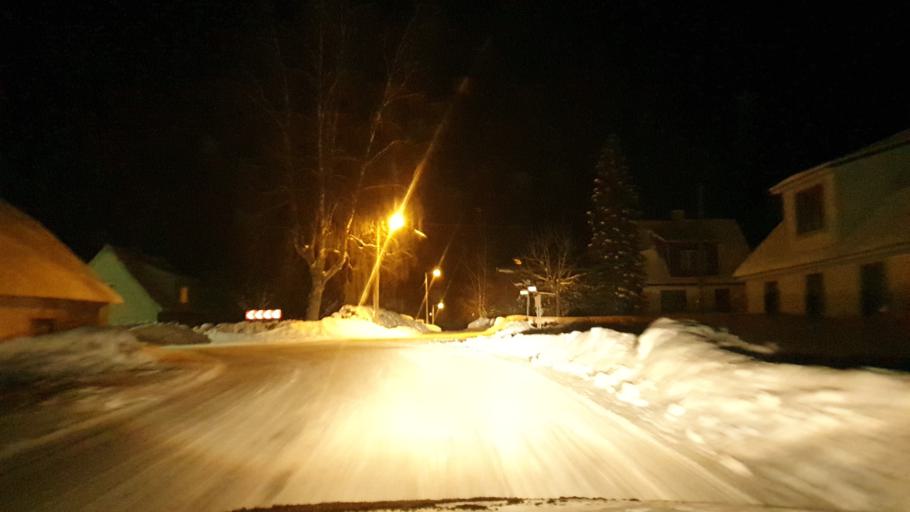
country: EE
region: Vorumaa
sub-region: Antsla vald
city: Vana-Antsla
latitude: 57.9822
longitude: 26.7619
